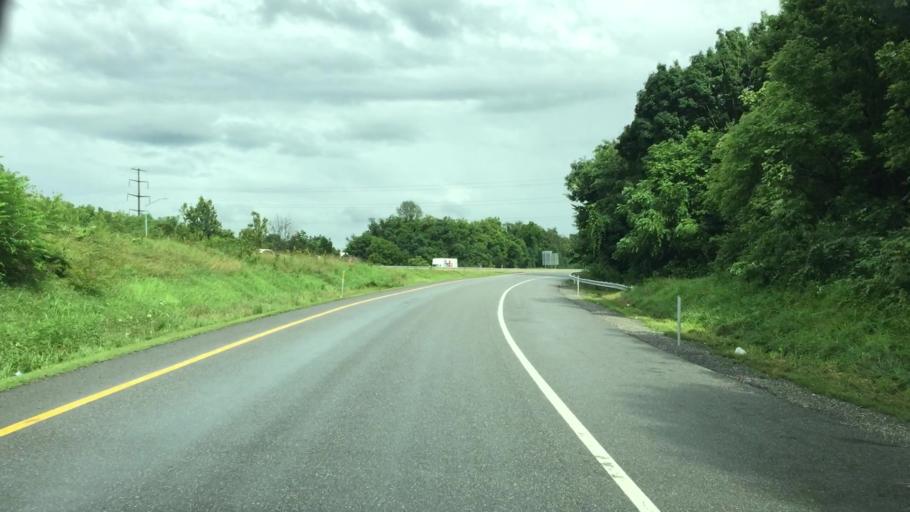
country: US
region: Maryland
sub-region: Washington County
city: Williamsport
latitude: 39.6287
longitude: -77.8077
